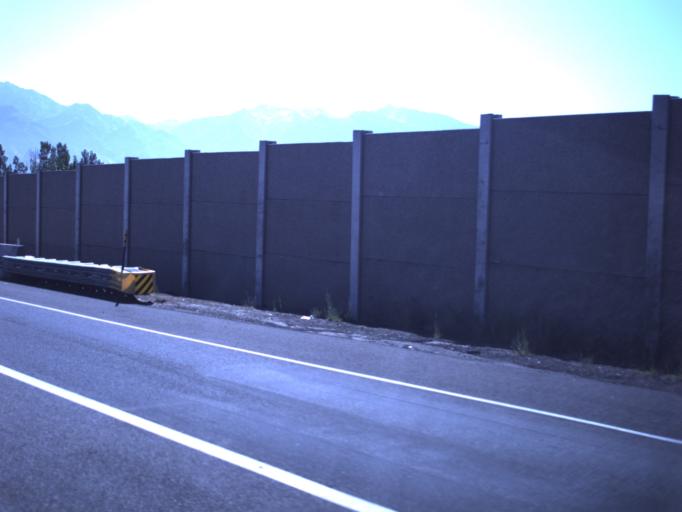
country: US
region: Utah
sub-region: Salt Lake County
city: Taylorsville
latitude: 40.6445
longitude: -111.9353
